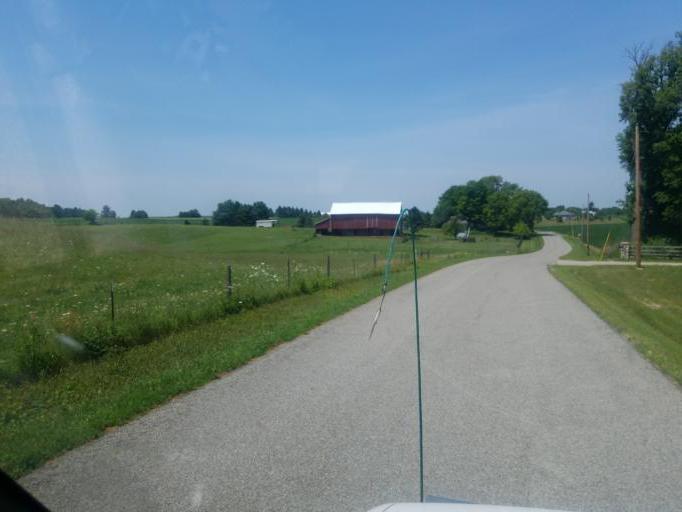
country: US
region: Ohio
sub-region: Logan County
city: West Liberty
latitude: 40.2918
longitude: -83.8226
